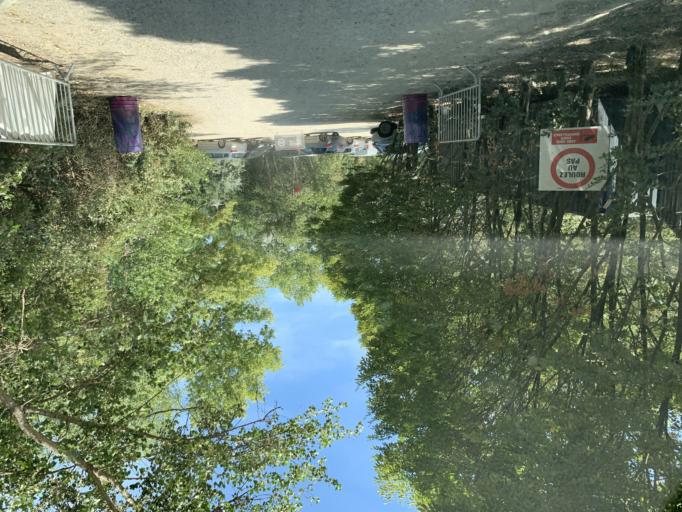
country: FR
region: Rhone-Alpes
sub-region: Departement du Rhone
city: Vaulx-en-Velin
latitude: 45.8054
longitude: 4.9315
